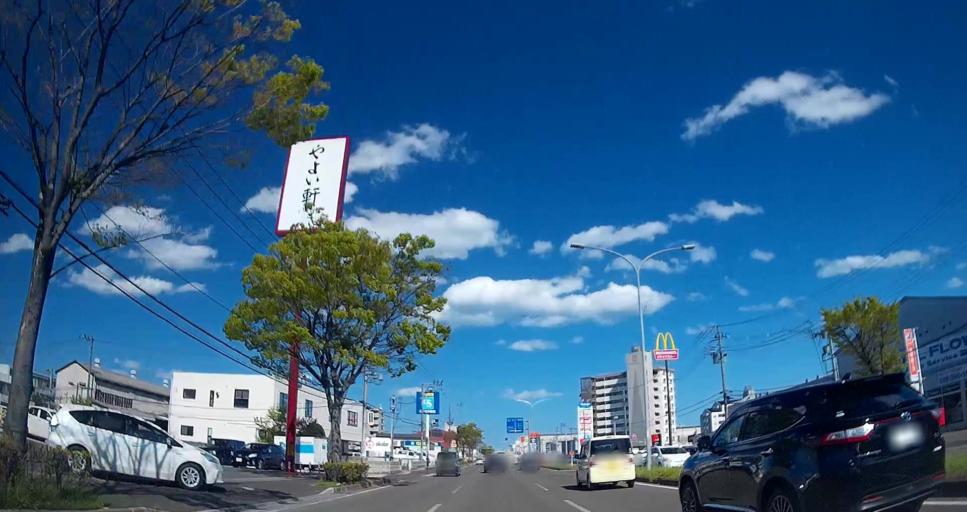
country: JP
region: Miyagi
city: Sendai-shi
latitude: 38.2511
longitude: 140.9330
